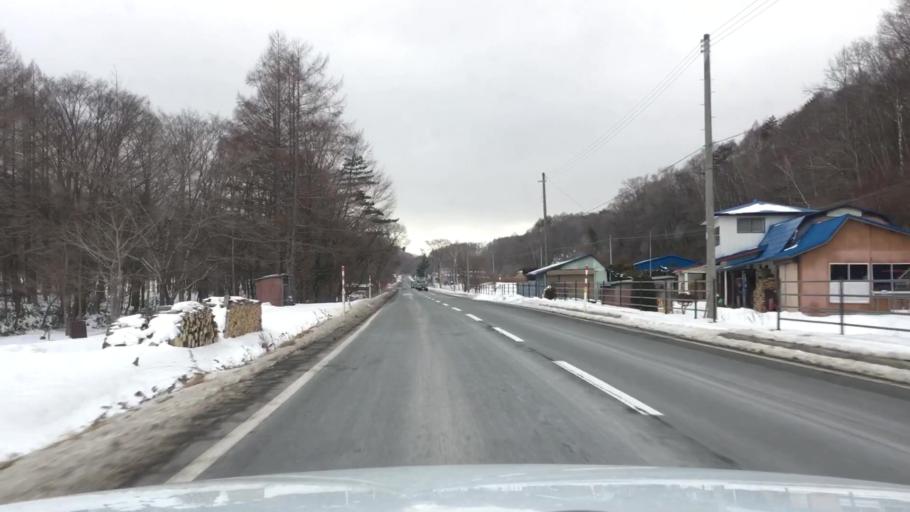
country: JP
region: Iwate
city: Morioka-shi
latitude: 39.6414
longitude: 141.4199
